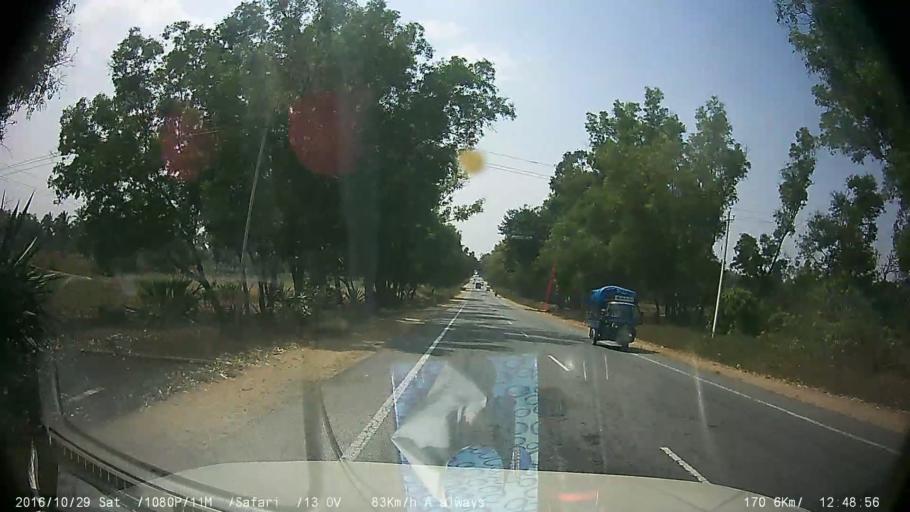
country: IN
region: Karnataka
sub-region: Mysore
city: Hunsur
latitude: 12.3298
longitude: 76.3696
